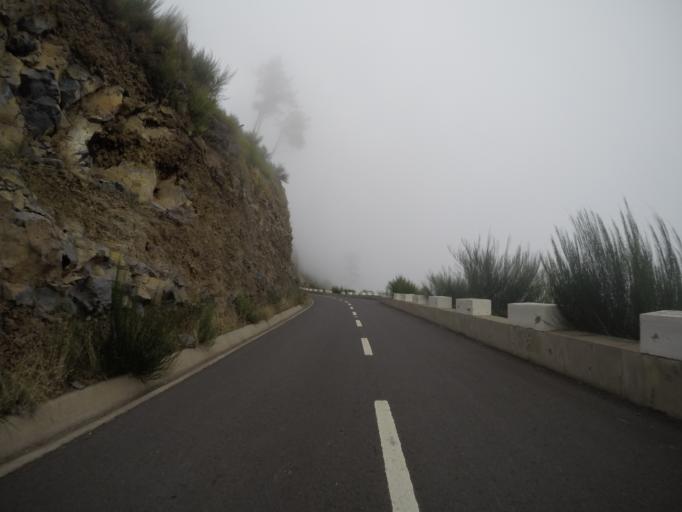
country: PT
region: Madeira
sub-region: Camara de Lobos
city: Curral das Freiras
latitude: 32.7087
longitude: -16.9551
